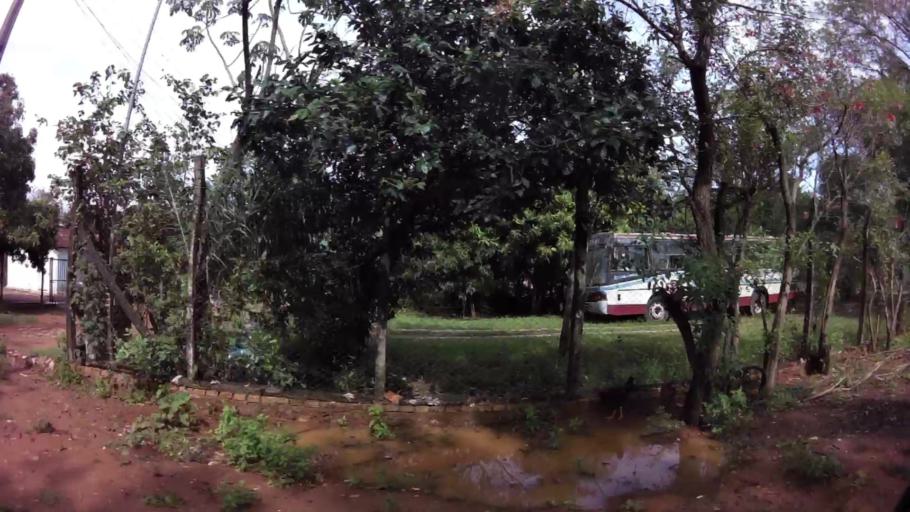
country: PY
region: Presidente Hayes
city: Villa Hayes
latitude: -25.1064
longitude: -57.4895
